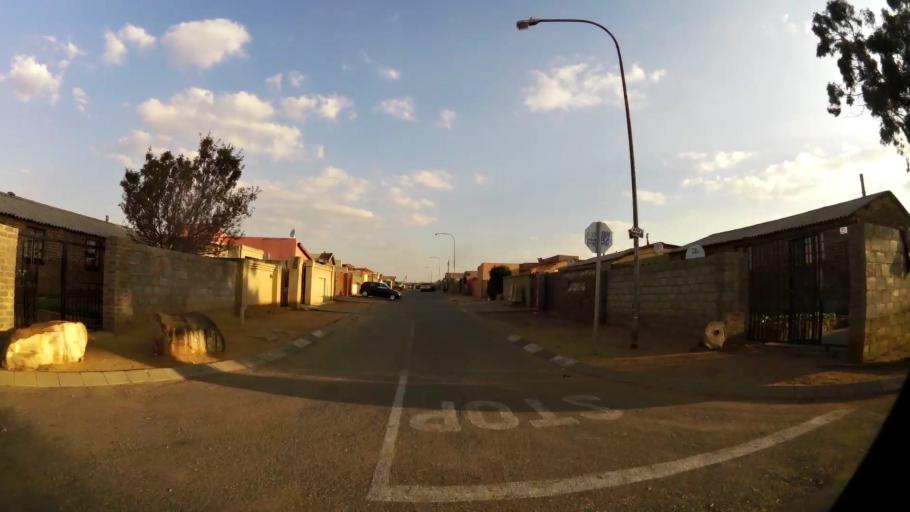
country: ZA
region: Gauteng
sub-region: City of Johannesburg Metropolitan Municipality
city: Roodepoort
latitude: -26.2101
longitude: 27.9021
